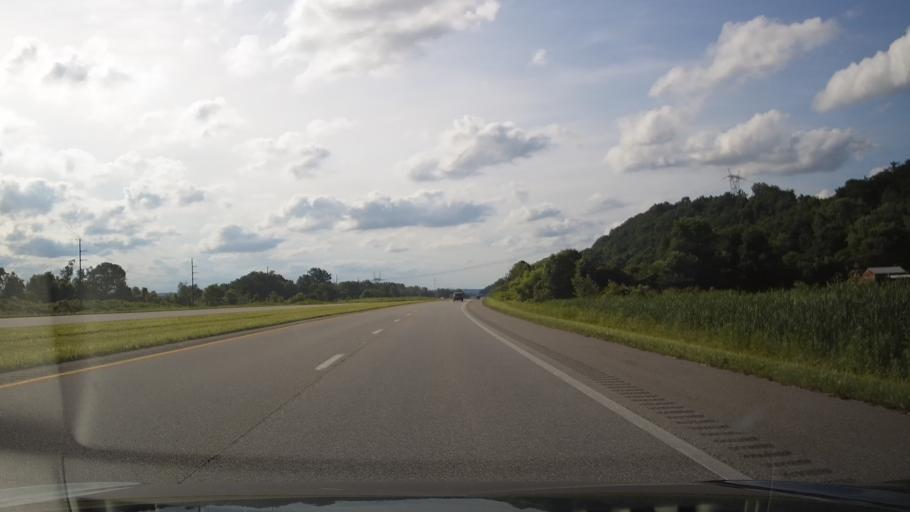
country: US
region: Kentucky
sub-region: Greenup County
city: Greenup
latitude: 38.6093
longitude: -82.8258
